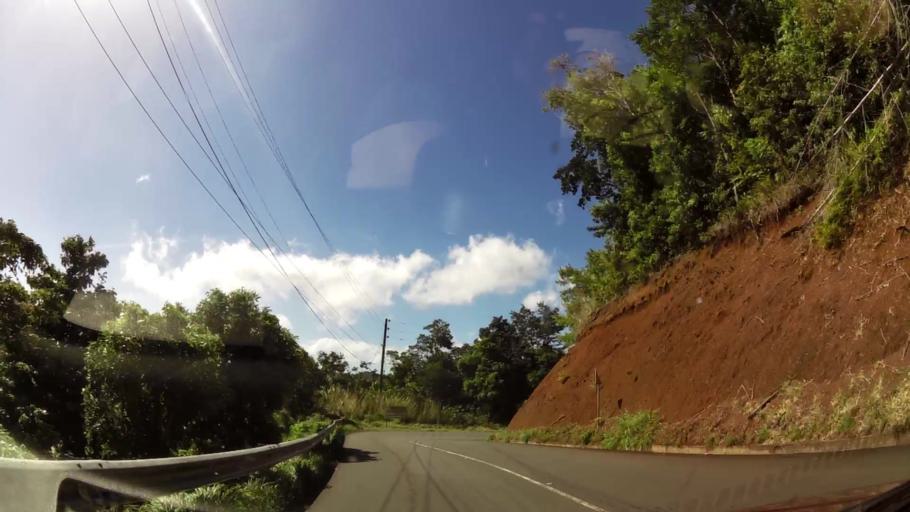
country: DM
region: Saint Paul
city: Pont Casse
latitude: 15.3512
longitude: -61.3600
